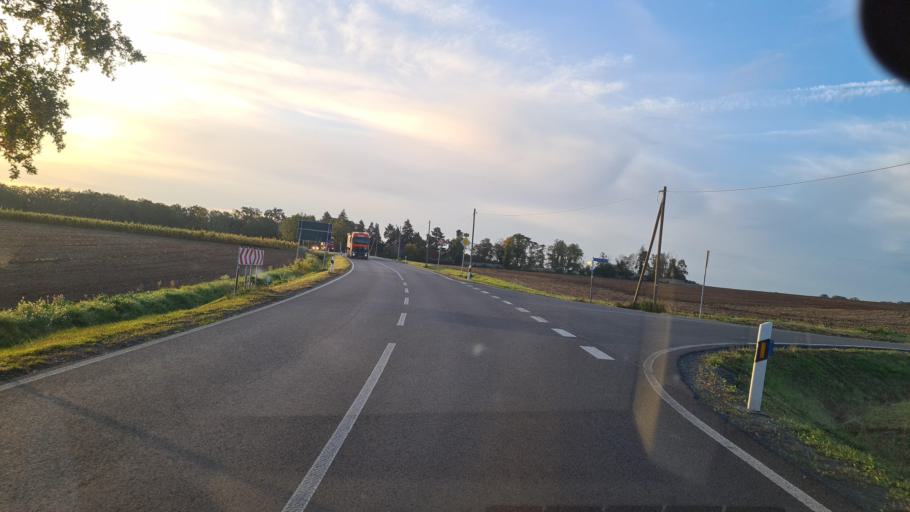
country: DE
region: Saxony
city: Machern
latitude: 51.3829
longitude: 12.6518
